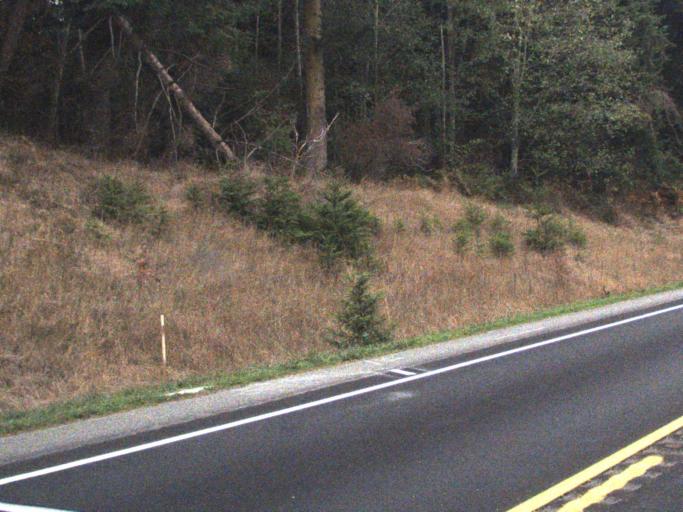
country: US
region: Washington
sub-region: Island County
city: Camano
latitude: 48.1326
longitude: -122.5904
